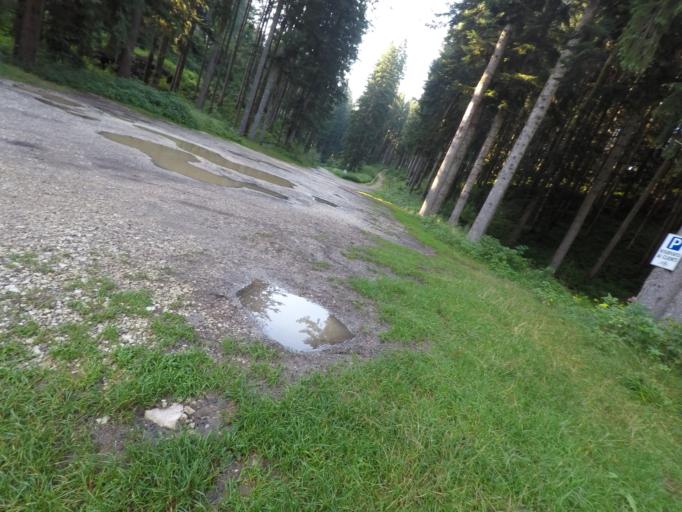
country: IT
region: Veneto
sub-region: Provincia di Vicenza
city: Asiago
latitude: 45.8583
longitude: 11.5283
